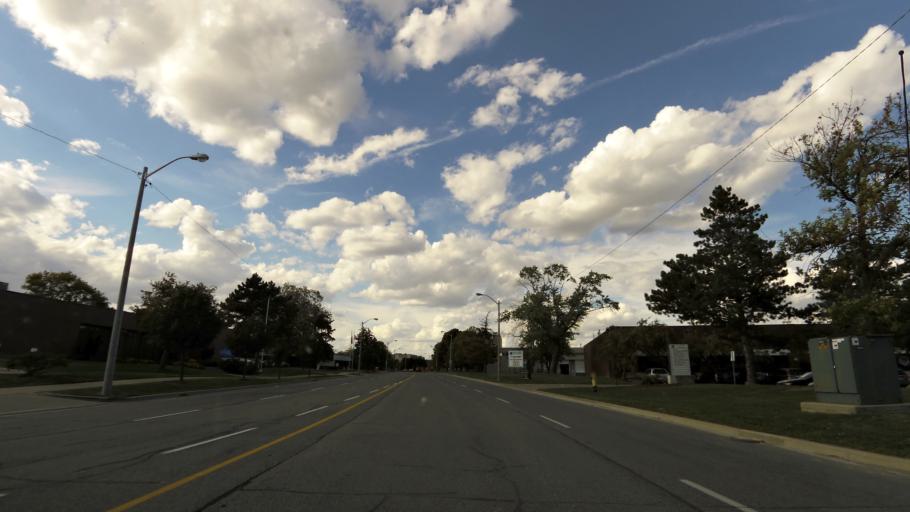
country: CA
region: Ontario
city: Etobicoke
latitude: 43.6128
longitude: -79.5161
